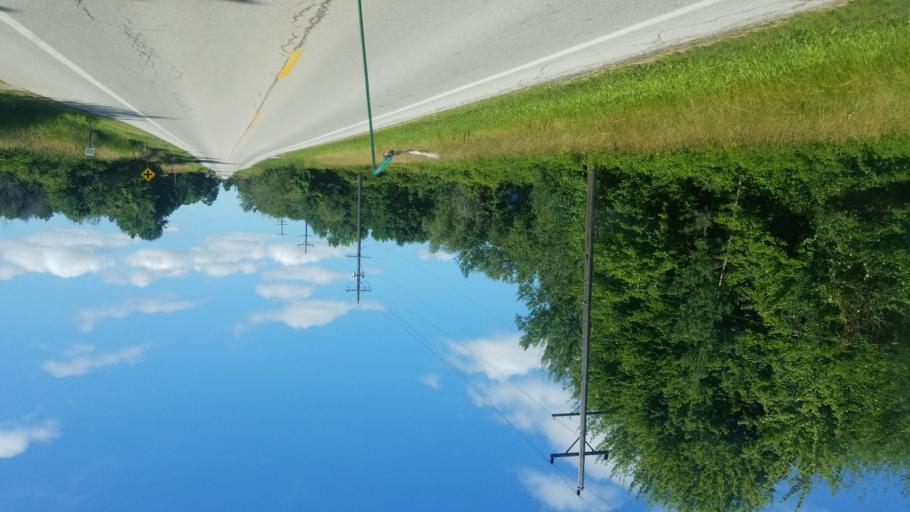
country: US
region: Ohio
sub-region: Ashtabula County
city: Conneaut
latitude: 41.8165
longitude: -80.5722
